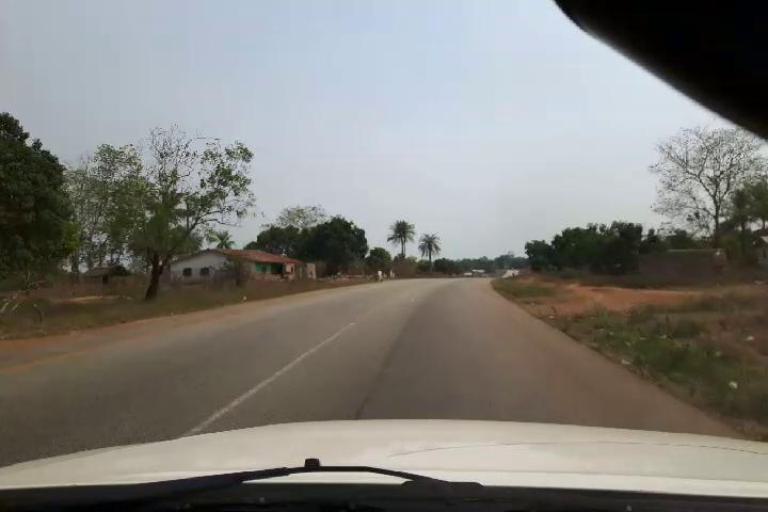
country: SL
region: Southern Province
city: Largo
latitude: 8.3157
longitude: -12.2176
